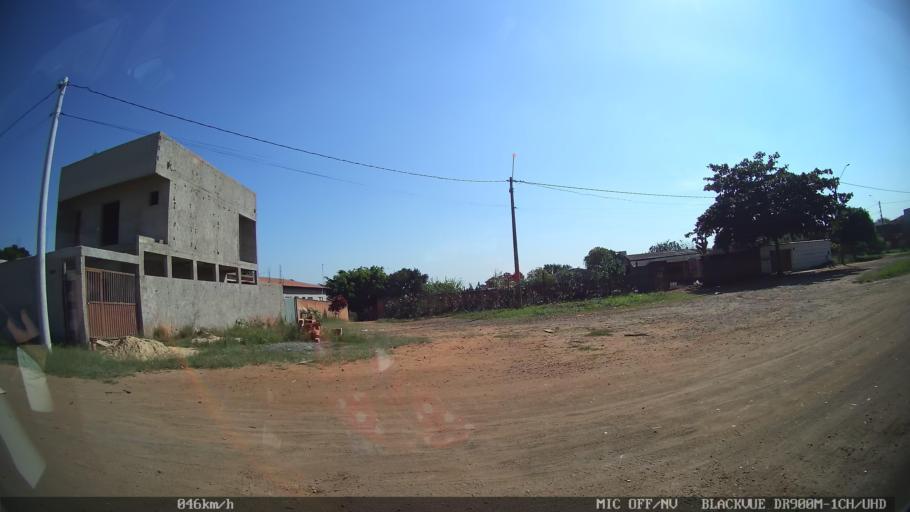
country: BR
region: Sao Paulo
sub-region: Valinhos
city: Valinhos
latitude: -23.0309
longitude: -47.0997
